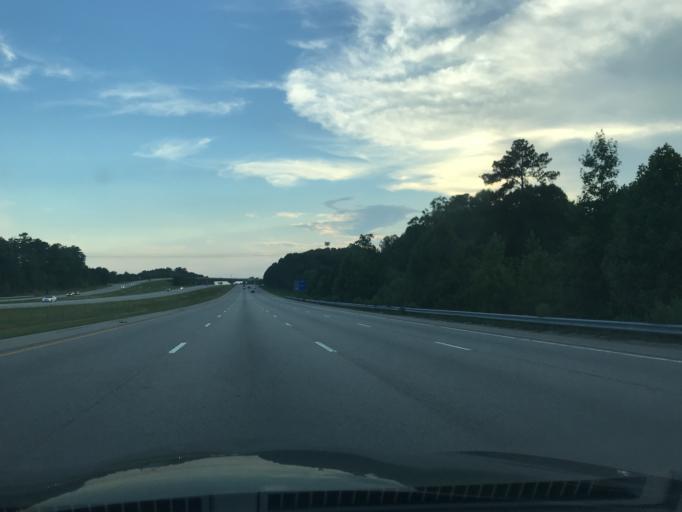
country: US
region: North Carolina
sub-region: Wake County
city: Morrisville
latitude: 35.9091
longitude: -78.7624
